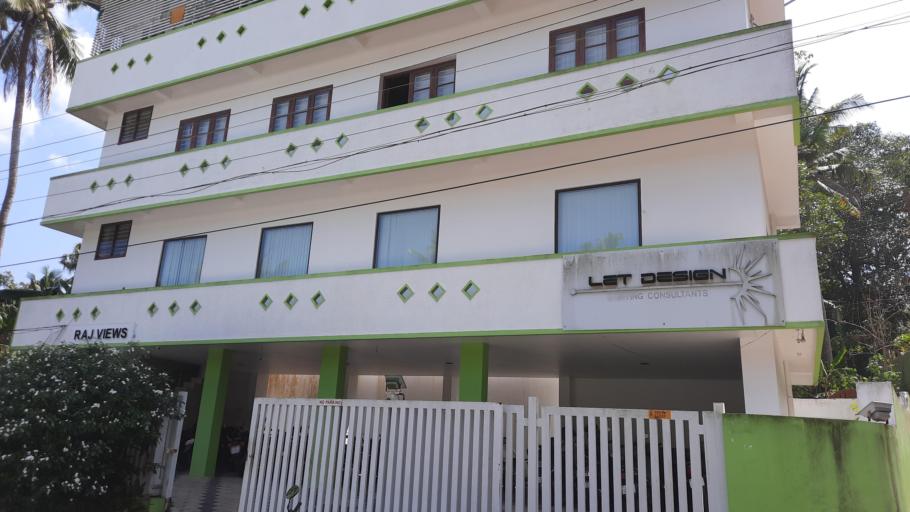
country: IN
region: Kerala
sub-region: Thiruvananthapuram
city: Thiruvananthapuram
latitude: 8.5547
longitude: 76.9303
